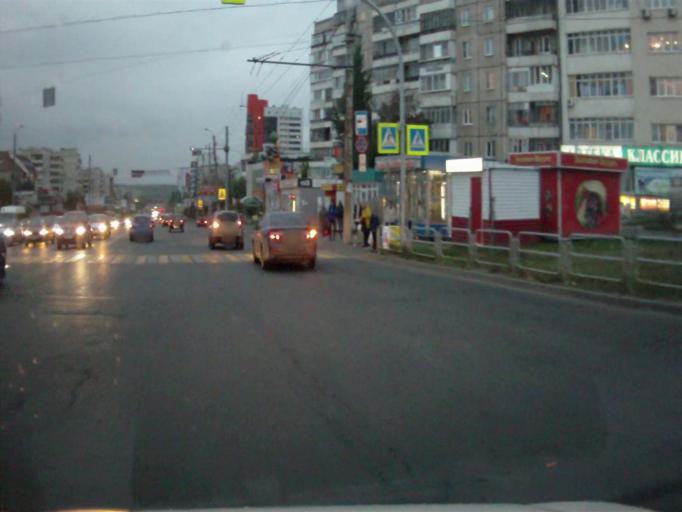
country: RU
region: Chelyabinsk
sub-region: Gorod Chelyabinsk
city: Chelyabinsk
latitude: 55.1886
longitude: 61.3326
